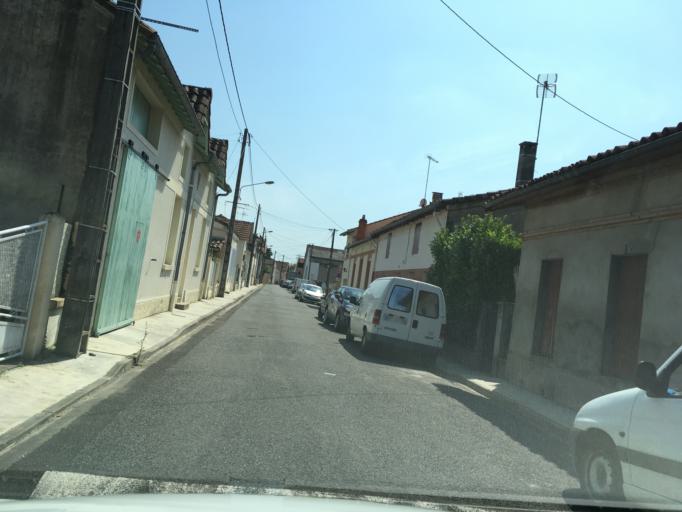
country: FR
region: Midi-Pyrenees
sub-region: Departement du Tarn-et-Garonne
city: Montauban
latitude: 44.0193
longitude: 1.3418
